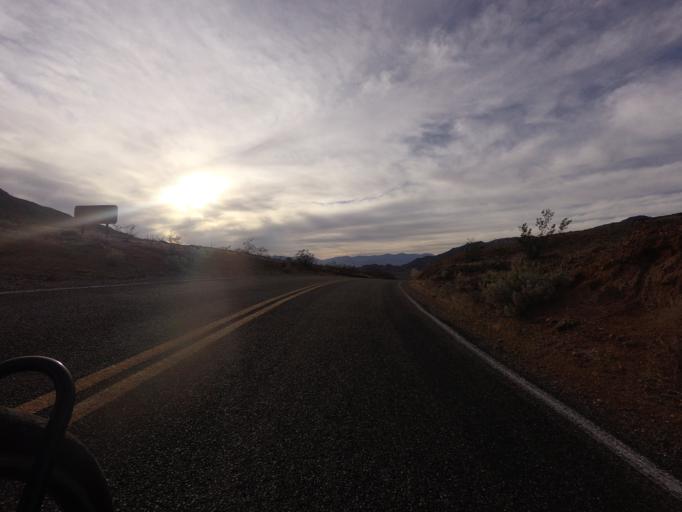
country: US
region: California
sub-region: San Bernardino County
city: Fort Irwin
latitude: 35.9099
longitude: -116.5789
